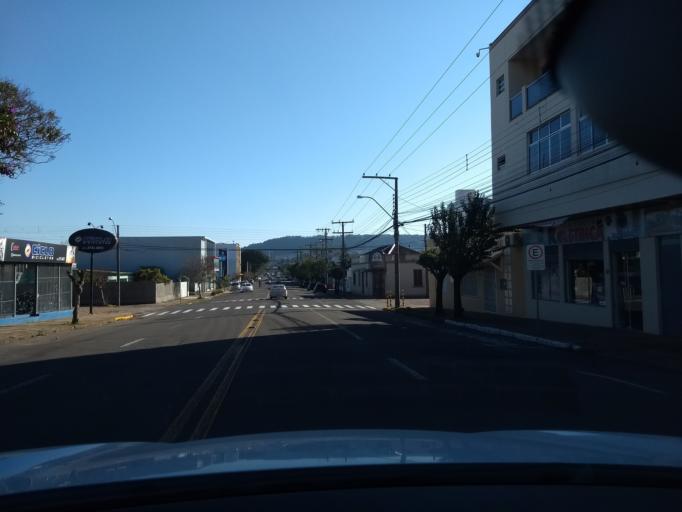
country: BR
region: Rio Grande do Sul
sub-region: Santa Cruz Do Sul
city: Santa Cruz do Sul
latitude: -29.7135
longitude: -52.4357
